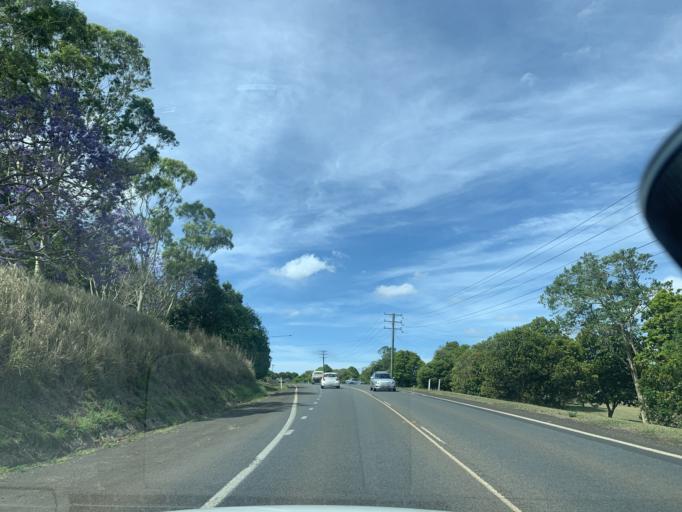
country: AU
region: Queensland
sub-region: Tablelands
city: Tolga
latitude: -17.2506
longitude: 145.4787
